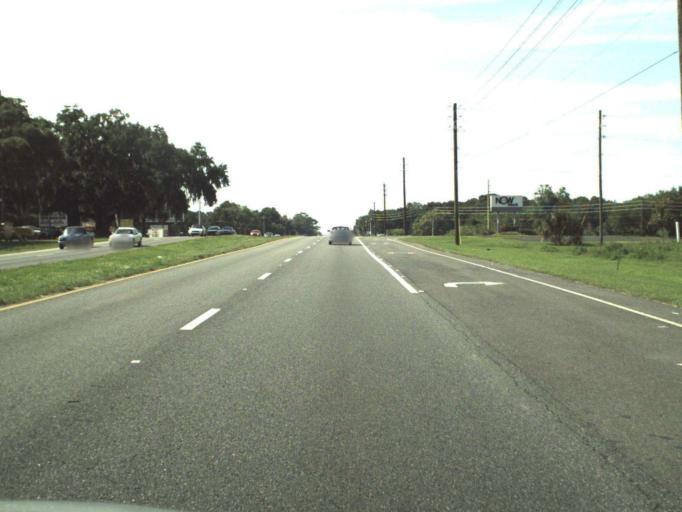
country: US
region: Florida
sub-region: Marion County
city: Belleview
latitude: 29.1216
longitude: -82.1000
